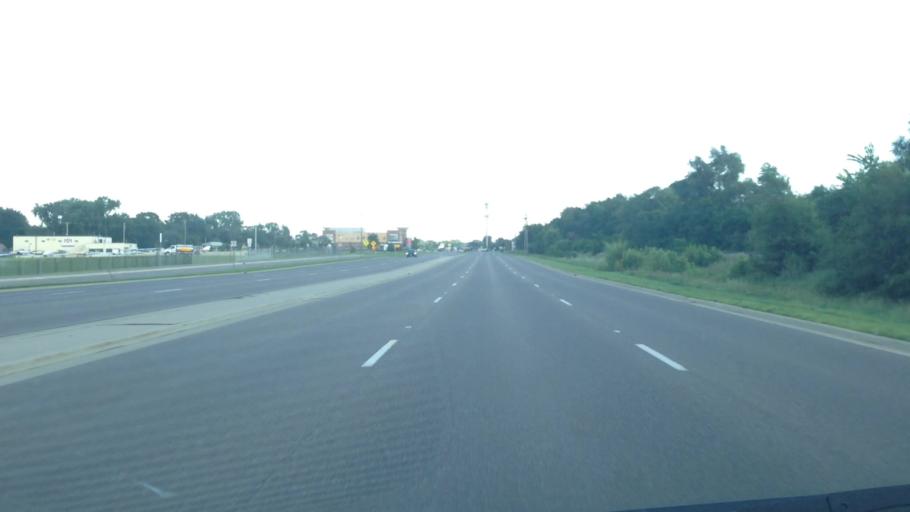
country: US
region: Minnesota
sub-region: Hennepin County
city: Crystal
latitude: 45.0605
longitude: -93.3624
